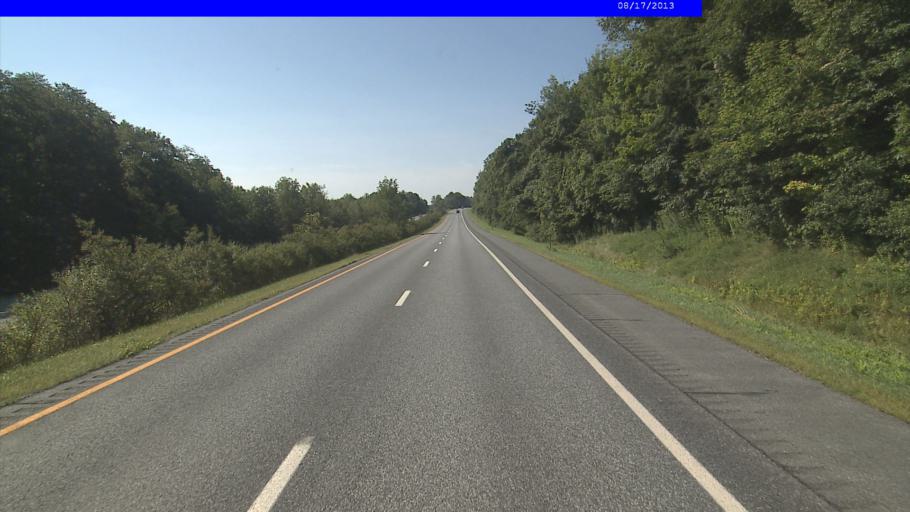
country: US
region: New Hampshire
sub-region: Sullivan County
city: Claremont
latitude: 43.3468
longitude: -72.4193
